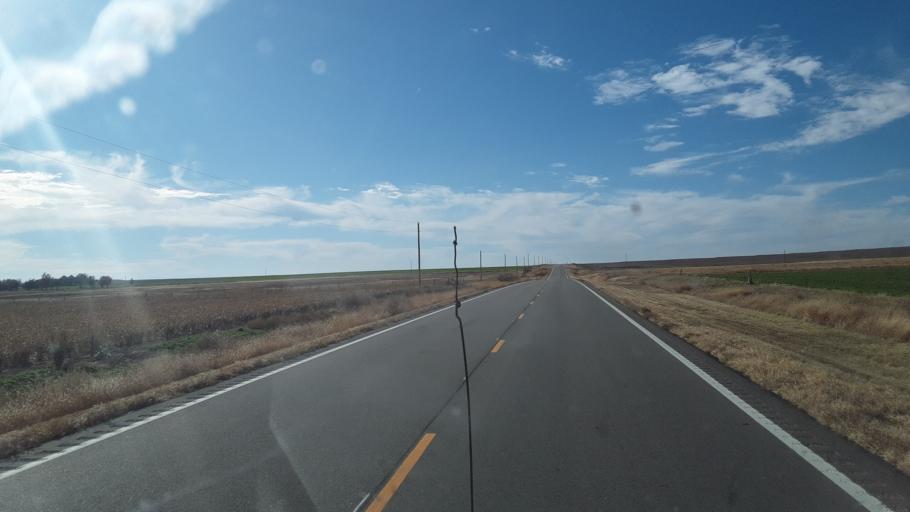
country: US
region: Kansas
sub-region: Hodgeman County
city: Jetmore
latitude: 38.0727
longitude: -100.0217
